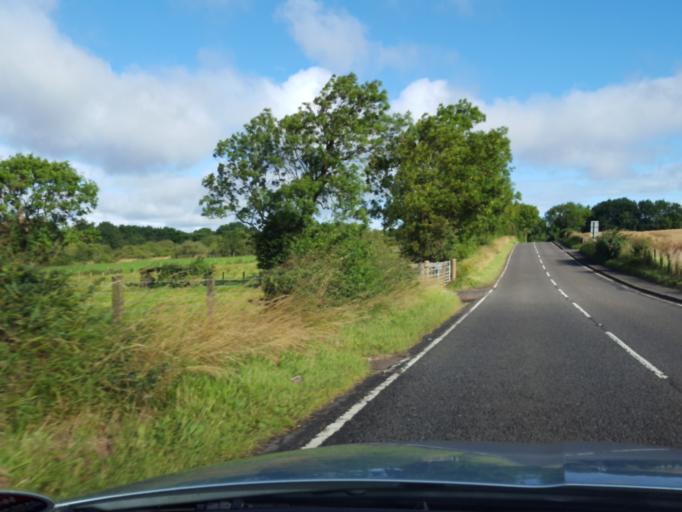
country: GB
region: Scotland
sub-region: West Lothian
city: Broxburn
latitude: 55.9372
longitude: -3.5078
